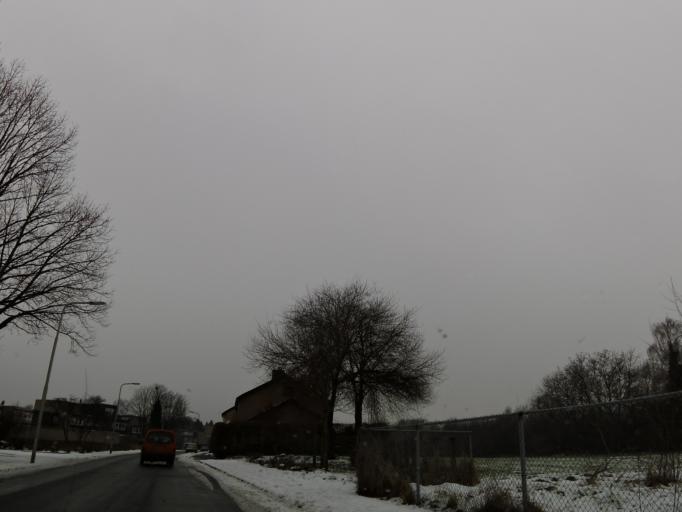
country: NL
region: Limburg
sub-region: Gemeente Kerkrade
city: Kerkrade
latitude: 50.8514
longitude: 6.0225
